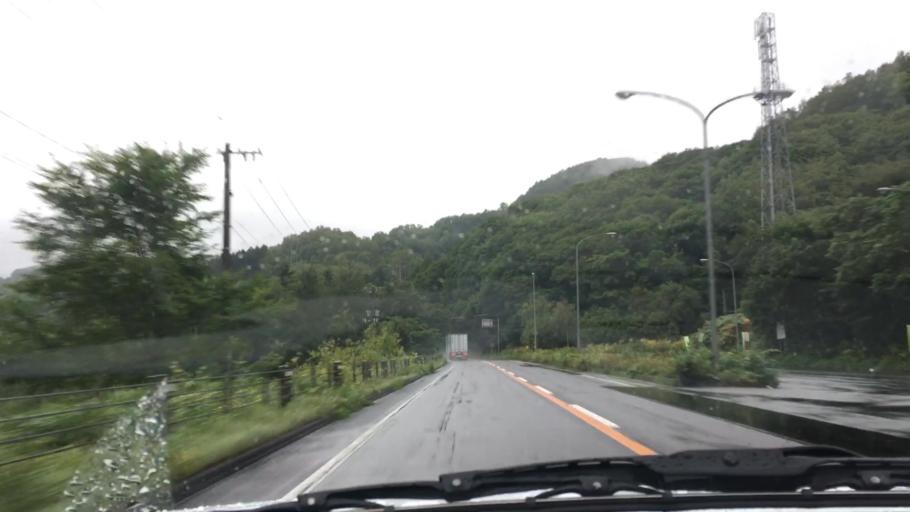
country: JP
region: Hokkaido
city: Niseko Town
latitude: 42.6025
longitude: 140.6188
